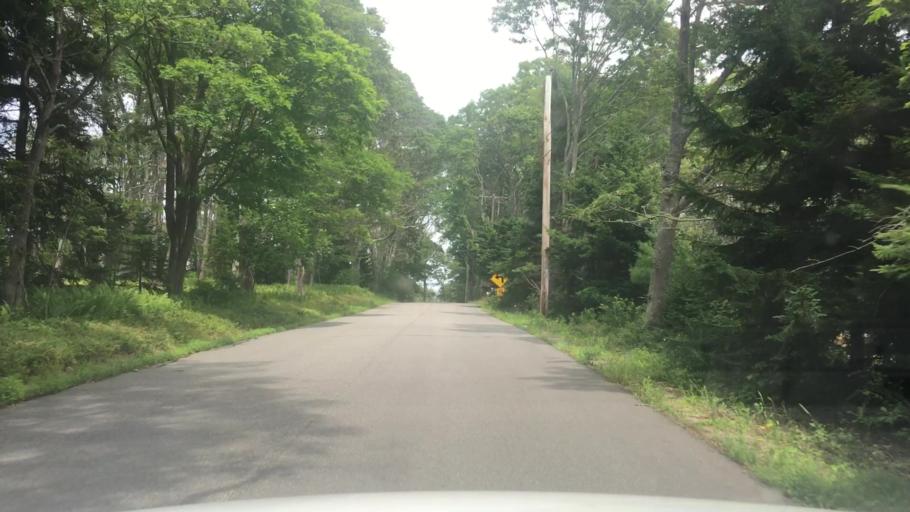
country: US
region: Maine
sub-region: Cumberland County
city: Scarborough
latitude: 43.5644
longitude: -70.2615
